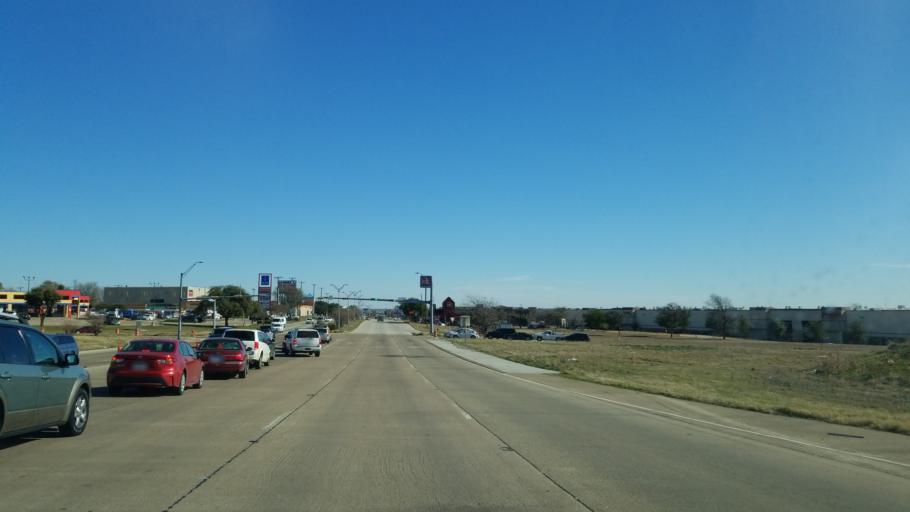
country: US
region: Texas
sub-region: Tarrant County
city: Arlington
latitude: 32.7122
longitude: -97.0621
